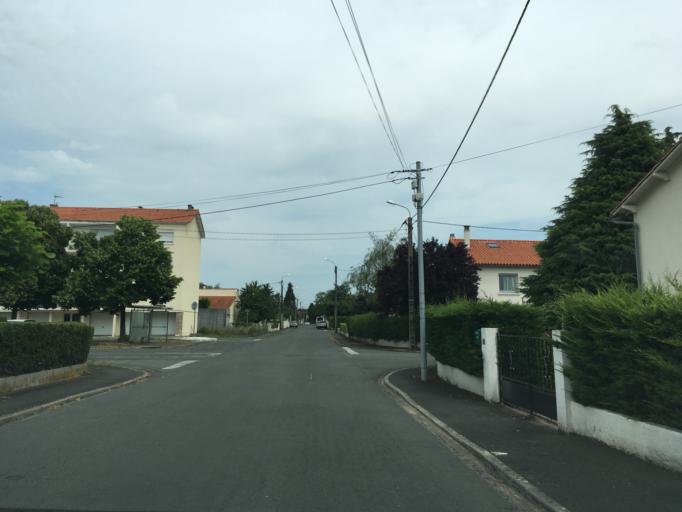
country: FR
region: Poitou-Charentes
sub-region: Departement des Deux-Sevres
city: Niort
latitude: 46.3080
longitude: -0.4708
